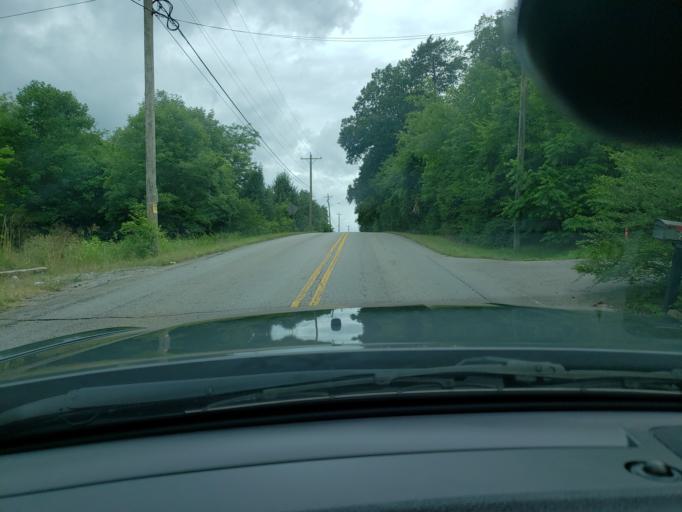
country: US
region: Tennessee
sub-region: Williamson County
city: Nolensville
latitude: 36.0227
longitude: -86.6812
